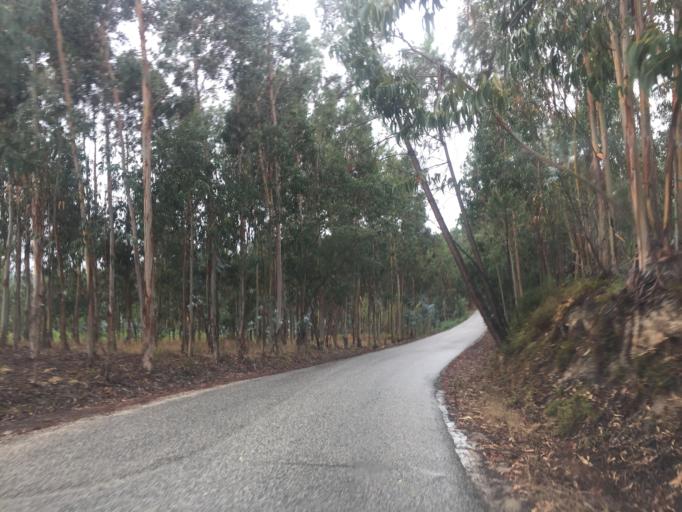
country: PT
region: Leiria
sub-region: Pombal
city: Lourical
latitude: 40.0524
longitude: -8.7765
